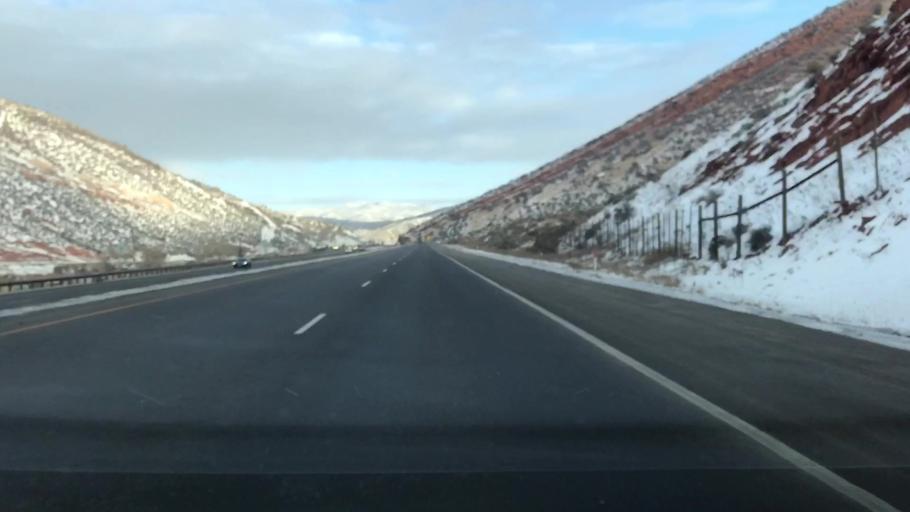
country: US
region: Colorado
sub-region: Eagle County
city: Edwards
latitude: 39.6679
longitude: -106.6442
